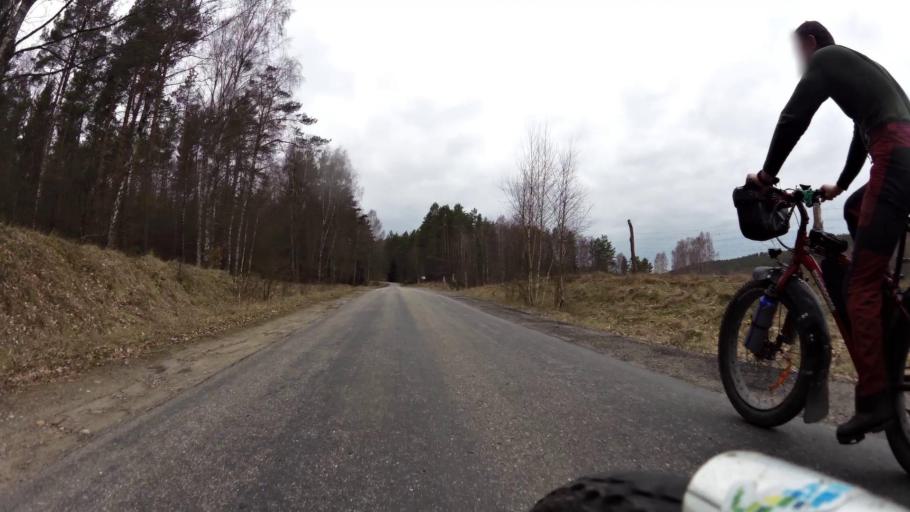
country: PL
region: Pomeranian Voivodeship
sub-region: Powiat bytowski
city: Trzebielino
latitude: 54.0855
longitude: 17.1266
